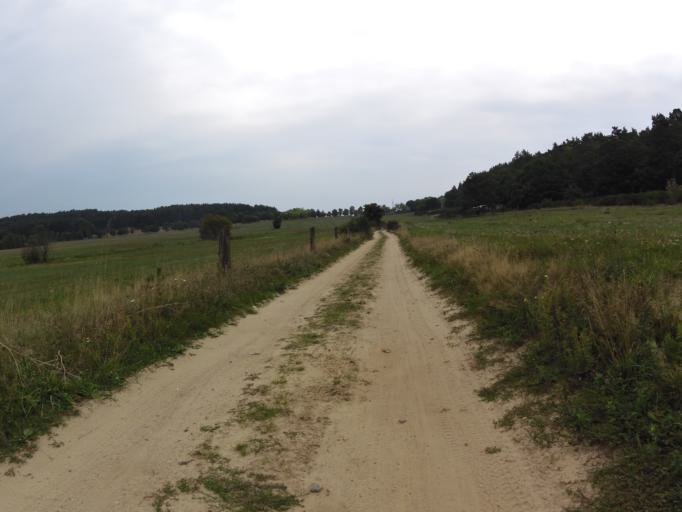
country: DE
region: Mecklenburg-Vorpommern
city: Seebad Heringsdorf
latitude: 53.9398
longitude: 14.1462
